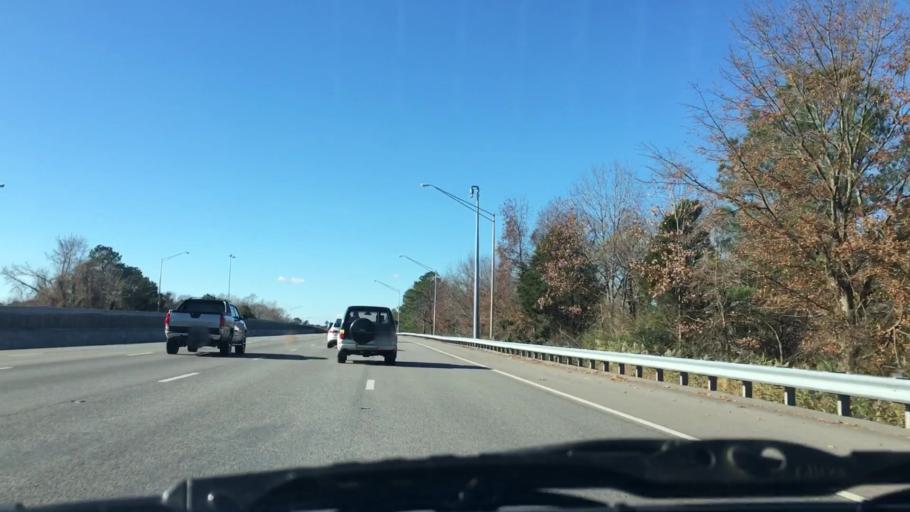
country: US
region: Virginia
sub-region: City of Virginia Beach
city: Virginia Beach
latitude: 36.8437
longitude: -76.0268
